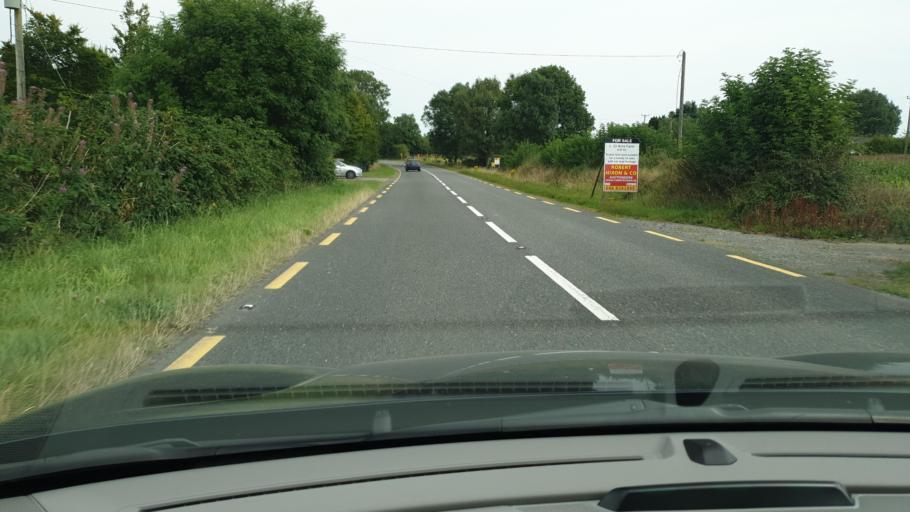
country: IE
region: Leinster
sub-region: An Mhi
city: Kells
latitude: 53.6934
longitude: -6.9474
